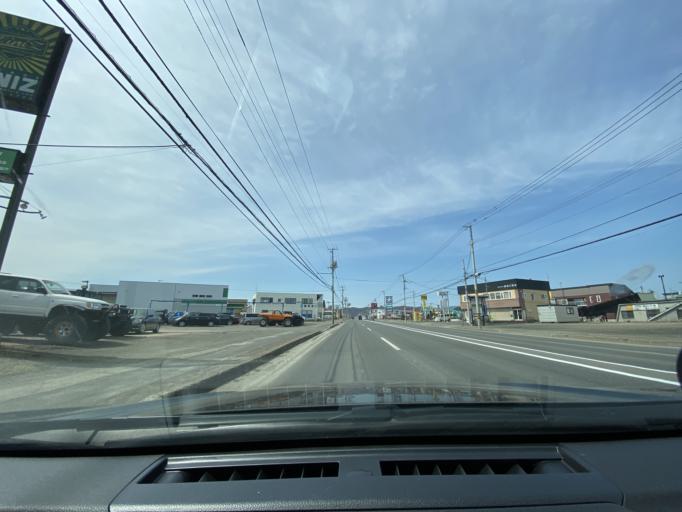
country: JP
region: Hokkaido
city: Kitami
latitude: 43.7986
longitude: 143.8313
